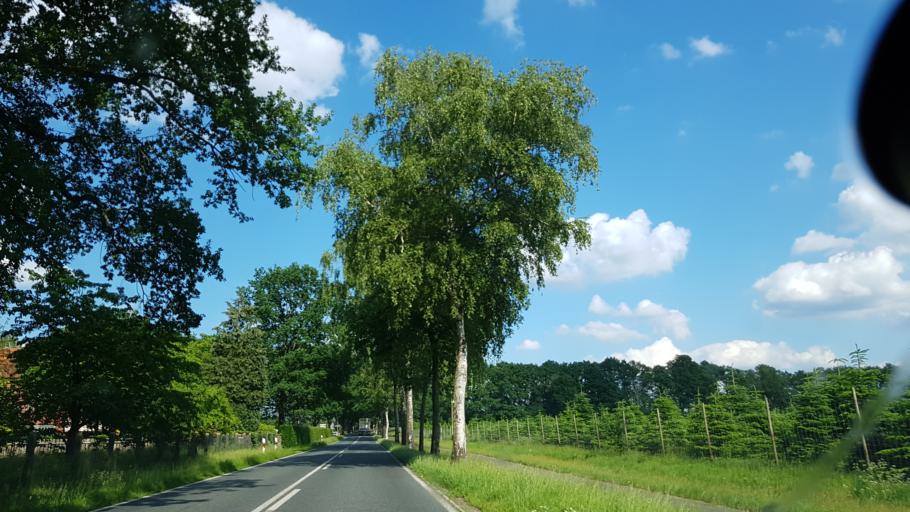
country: DE
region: Lower Saxony
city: Wenzendorf
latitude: 53.3468
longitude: 9.7943
